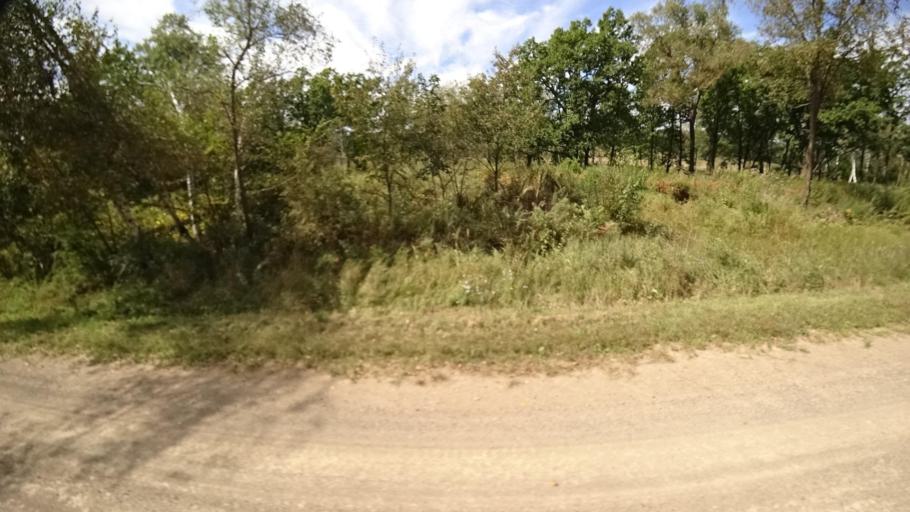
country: RU
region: Primorskiy
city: Yakovlevka
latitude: 44.6879
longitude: 133.6183
